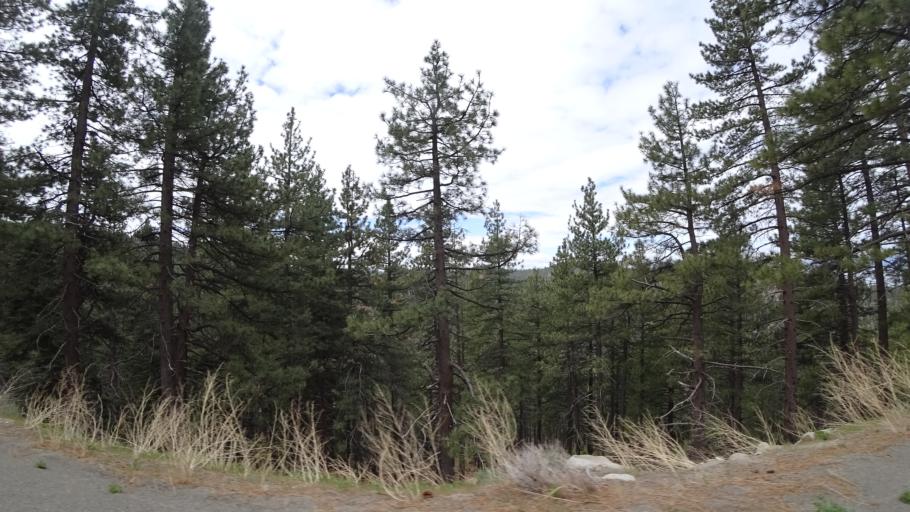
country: US
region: Nevada
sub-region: Washoe County
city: Incline Village
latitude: 39.1210
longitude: -119.9281
